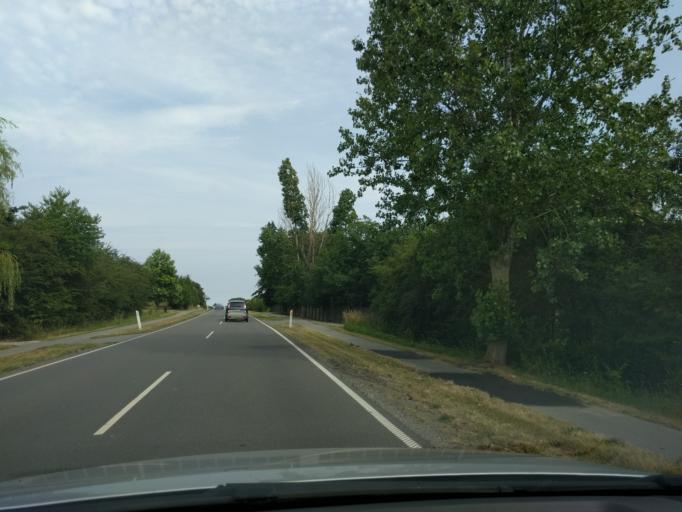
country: DK
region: South Denmark
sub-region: Nordfyns Kommune
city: Otterup
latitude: 55.5584
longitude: 10.4511
